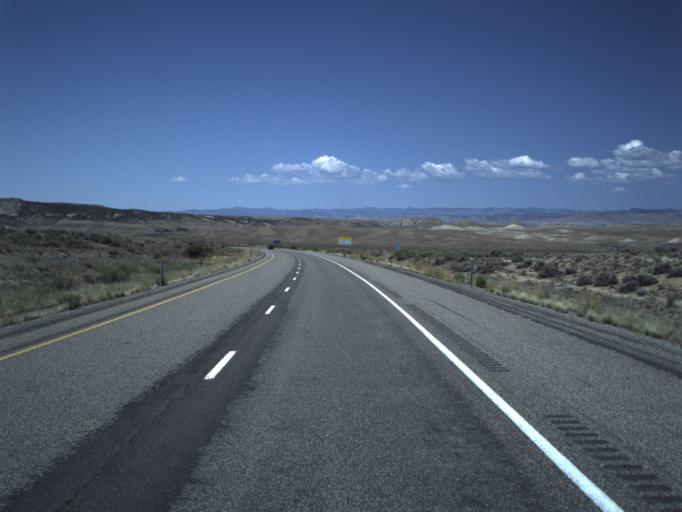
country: US
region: Colorado
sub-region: Mesa County
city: Loma
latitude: 39.1954
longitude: -109.0625
